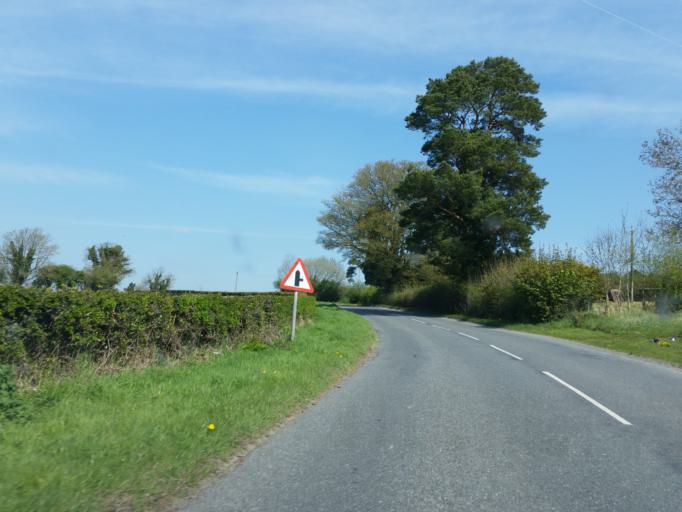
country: GB
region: Northern Ireland
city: Lisnaskea
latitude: 54.2656
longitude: -7.4466
